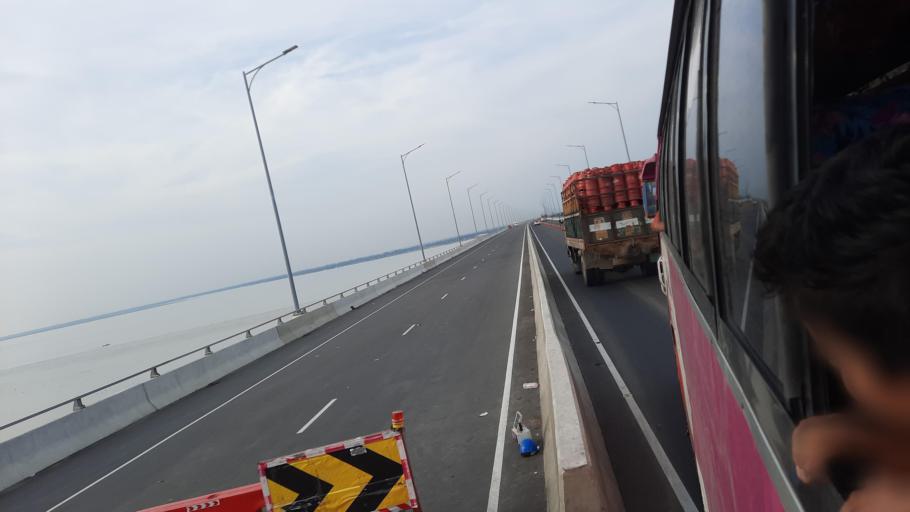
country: BD
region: Dhaka
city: Char Bhadrasan
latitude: 23.4435
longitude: 90.2613
